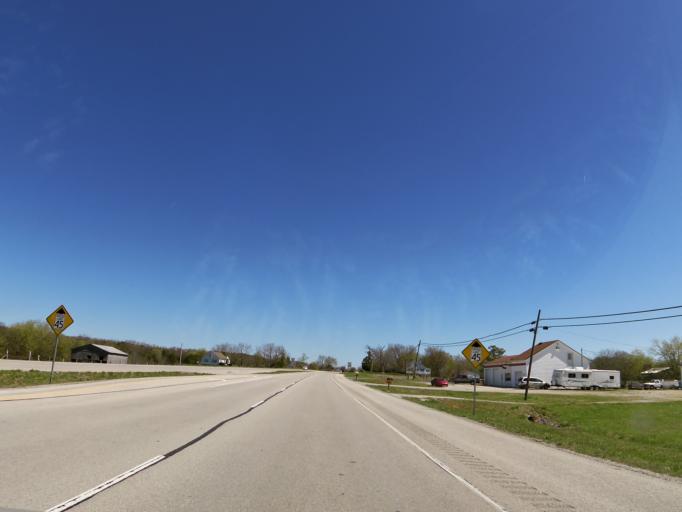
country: US
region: Kentucky
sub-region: Warren County
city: Bowling Green
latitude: 36.9229
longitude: -86.5546
